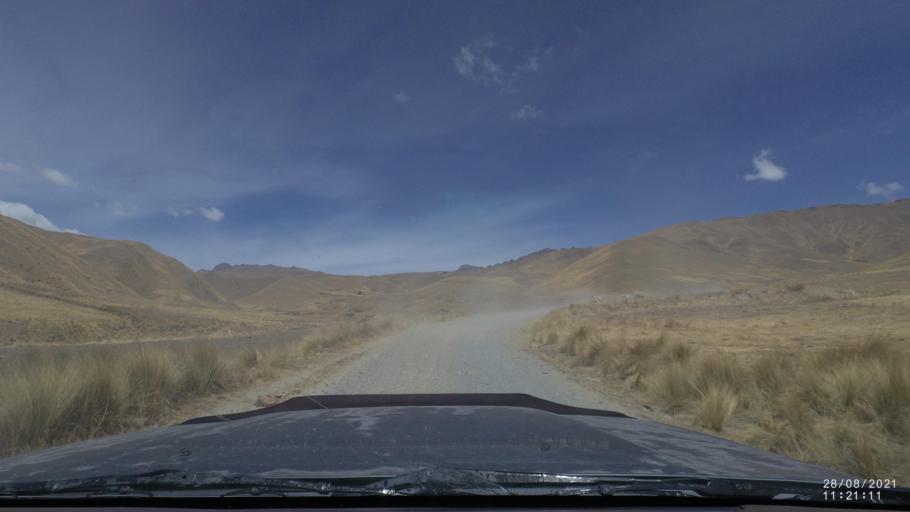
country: BO
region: Cochabamba
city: Sipe Sipe
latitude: -17.1638
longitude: -66.3454
